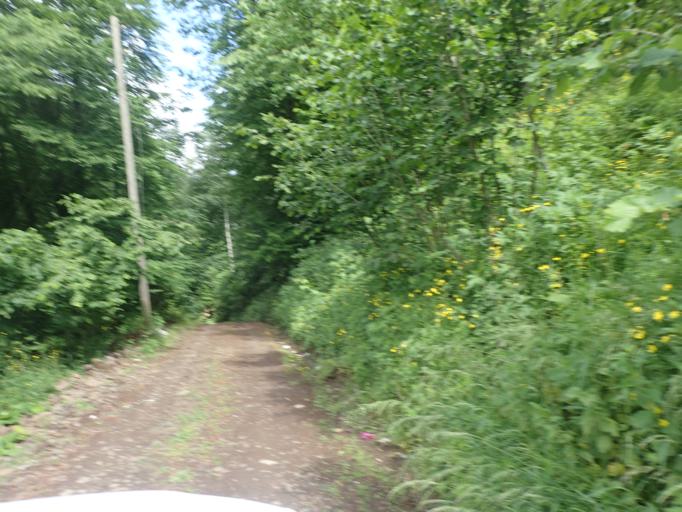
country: TR
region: Samsun
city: Salipazari
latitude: 40.9411
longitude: 36.8540
